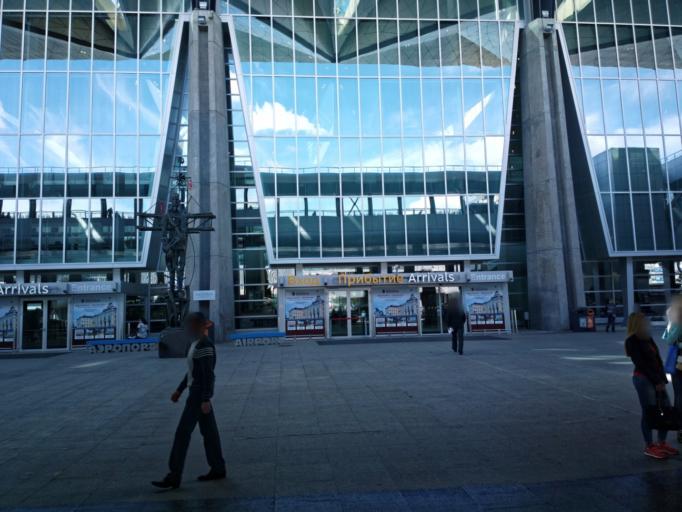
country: RU
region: St.-Petersburg
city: Dachnoye
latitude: 59.7996
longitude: 30.2738
